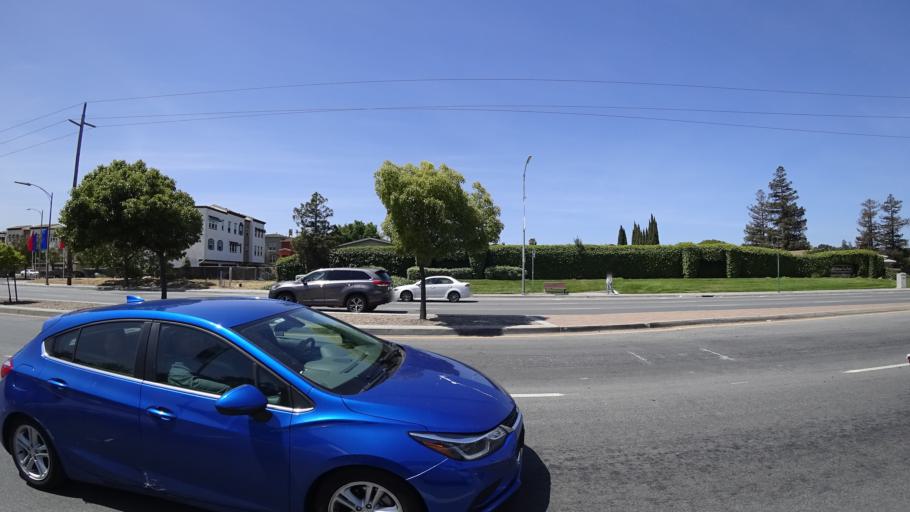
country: US
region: California
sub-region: Santa Clara County
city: Seven Trees
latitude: 37.2942
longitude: -121.8518
